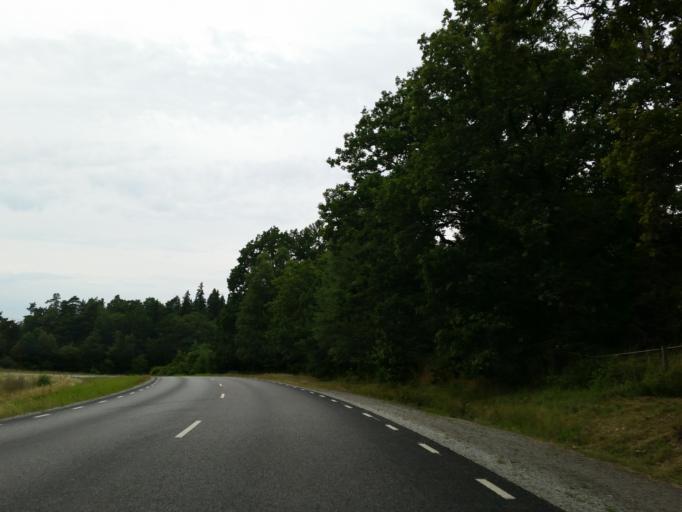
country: SE
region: Stockholm
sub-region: Salems Kommun
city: Ronninge
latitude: 59.2324
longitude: 17.7076
